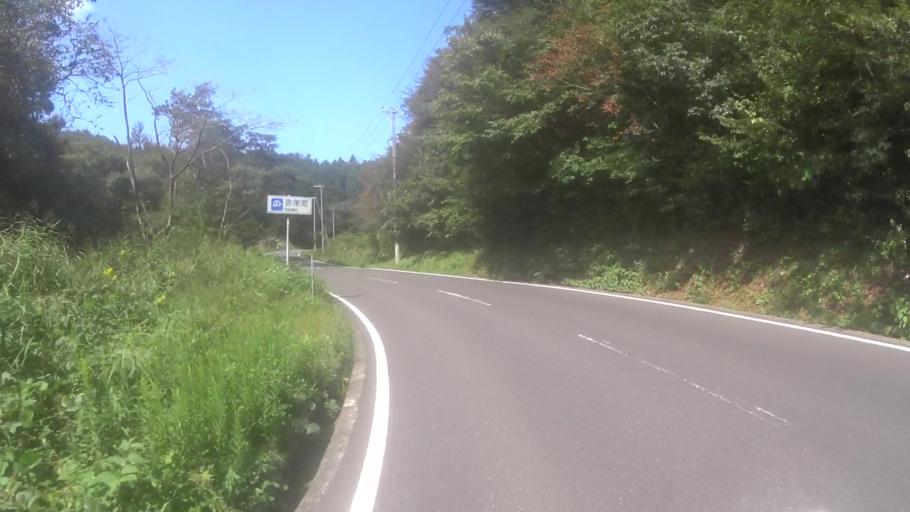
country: JP
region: Kyoto
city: Miyazu
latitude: 35.6231
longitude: 135.1273
